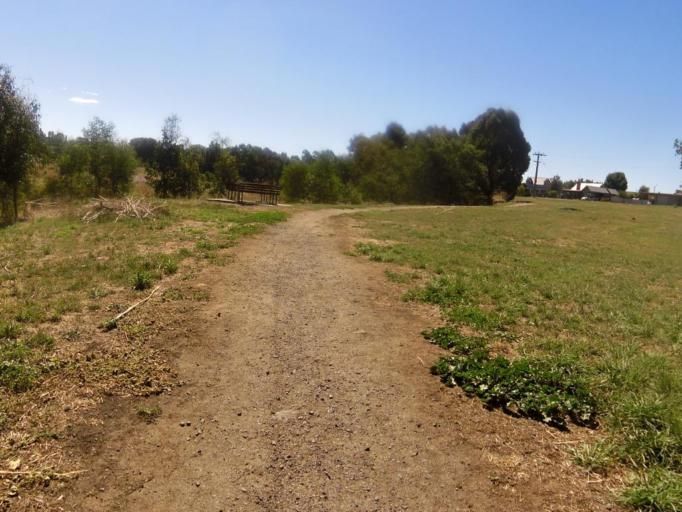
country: AU
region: Victoria
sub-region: Mount Alexander
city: Castlemaine
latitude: -37.2456
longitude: 144.4445
